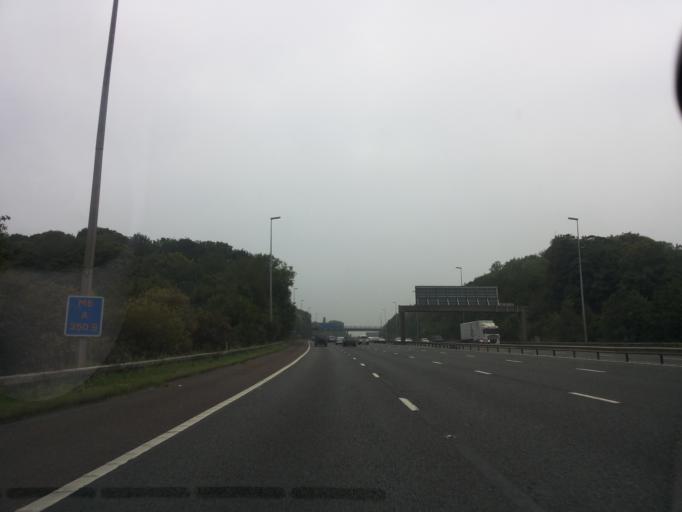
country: GB
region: England
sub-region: Lancashire
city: Goosnargh
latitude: 53.7736
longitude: -2.6412
